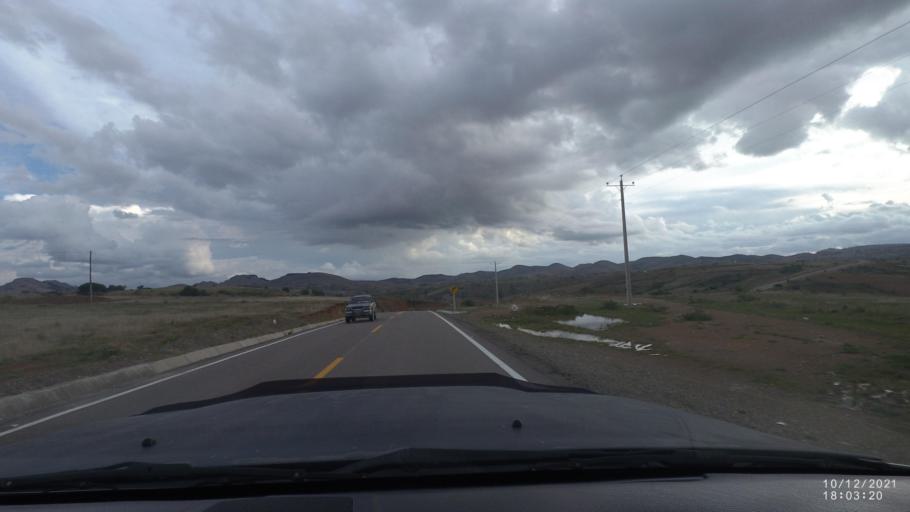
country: BO
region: Cochabamba
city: Cliza
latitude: -17.7586
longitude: -65.9187
